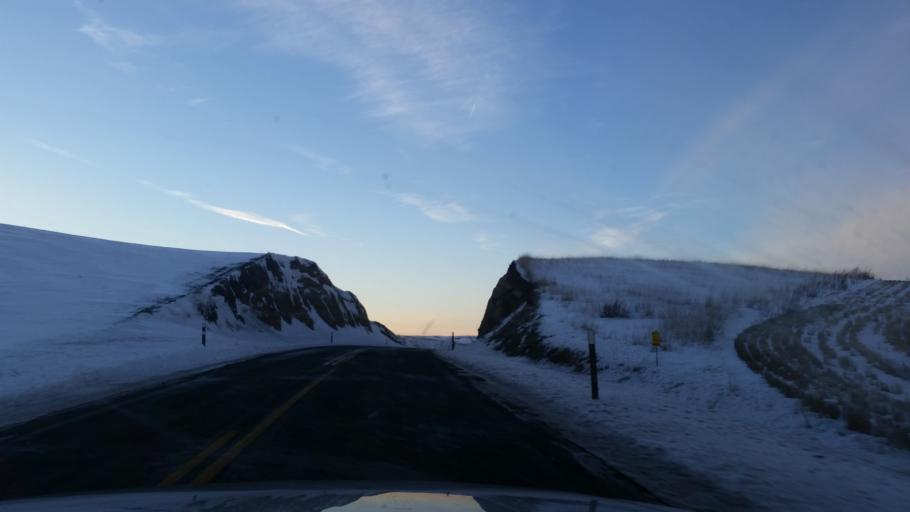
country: US
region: Washington
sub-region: Spokane County
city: Cheney
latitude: 47.1555
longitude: -117.8586
